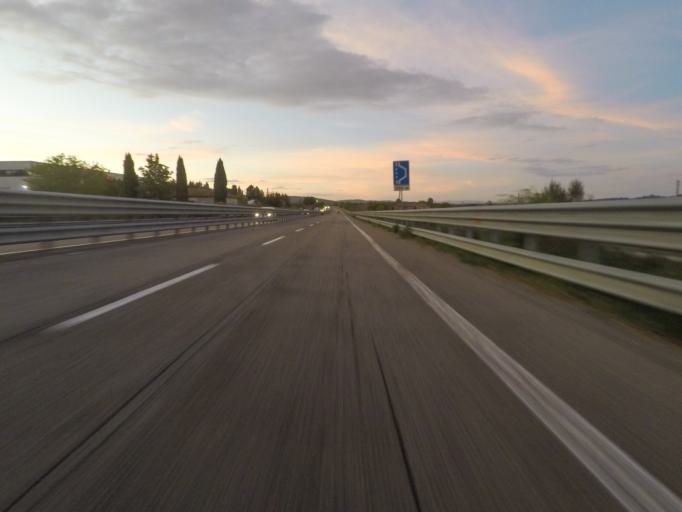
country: IT
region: Tuscany
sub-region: Provincia di Siena
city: Sinalunga
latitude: 43.2327
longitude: 11.7299
